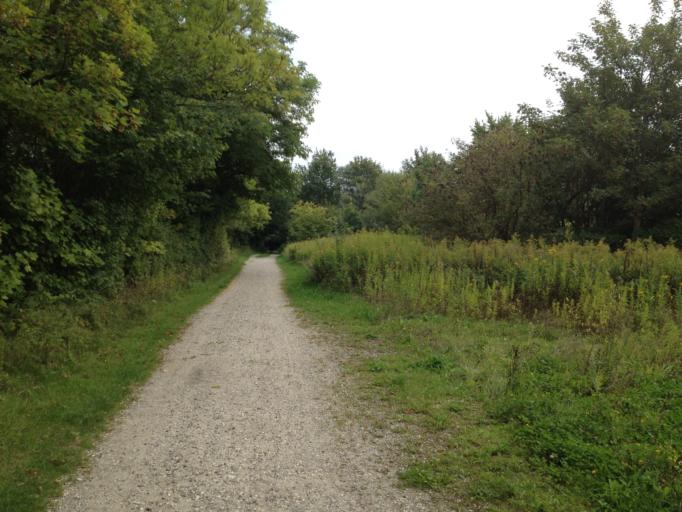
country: DK
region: Capital Region
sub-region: Fredensborg Kommune
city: Niva
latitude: 55.9407
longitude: 12.5133
